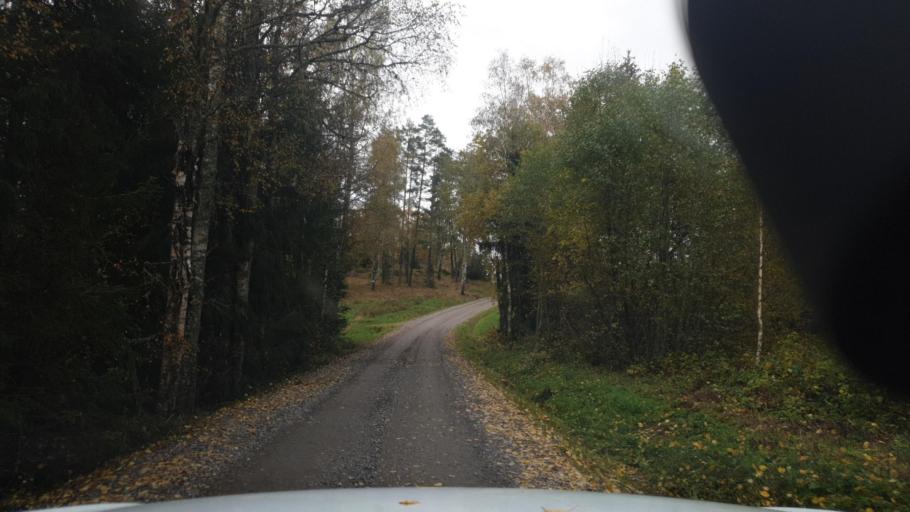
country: SE
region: Vaermland
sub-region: Karlstads Kommun
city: Edsvalla
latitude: 59.4706
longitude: 13.1272
